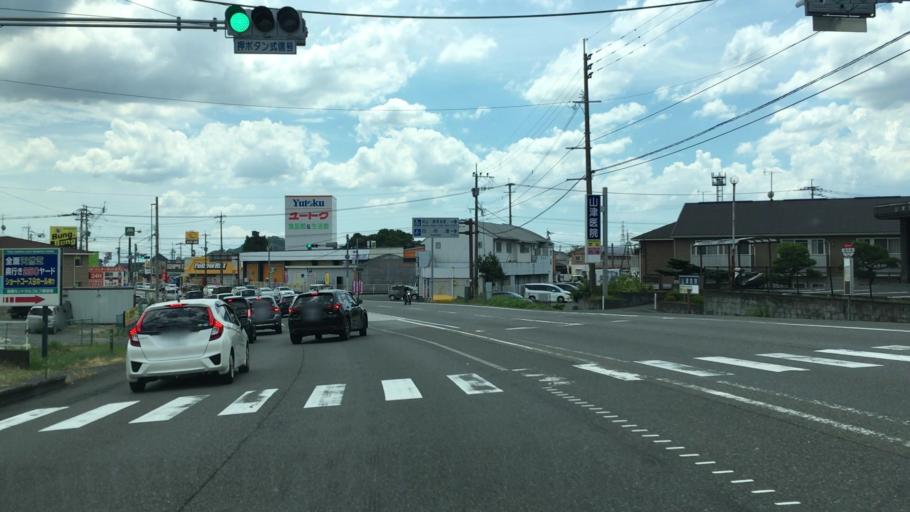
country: JP
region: Saga Prefecture
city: Tosu
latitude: 33.3902
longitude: 130.5004
